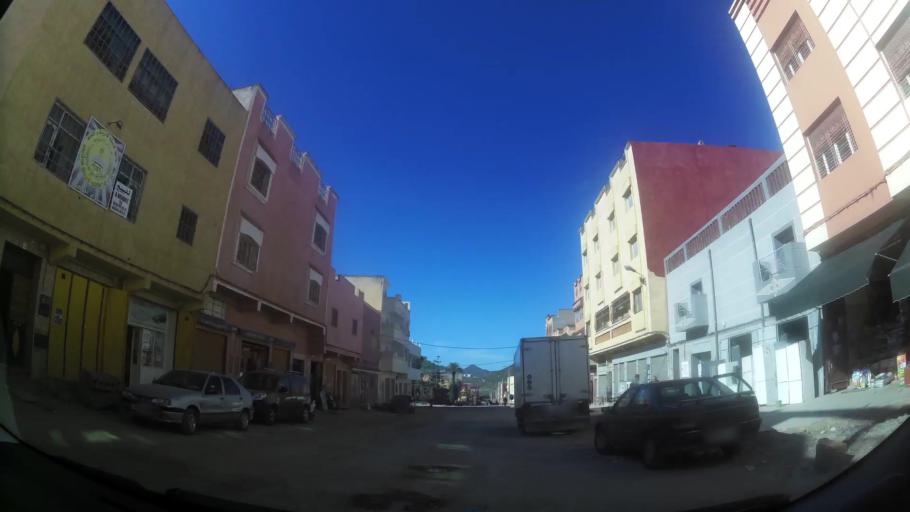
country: MA
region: Oriental
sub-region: Berkane-Taourirt
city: Ahfir
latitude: 34.9536
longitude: -2.0992
